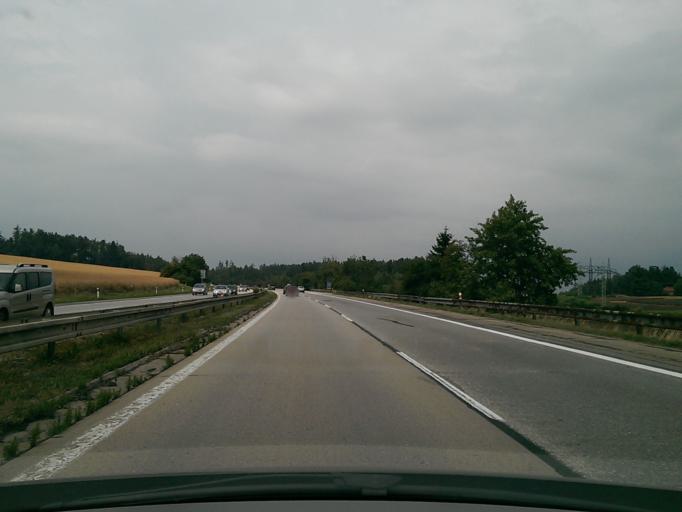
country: CZ
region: South Moravian
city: Zbraslav
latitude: 49.2557
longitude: 16.3442
